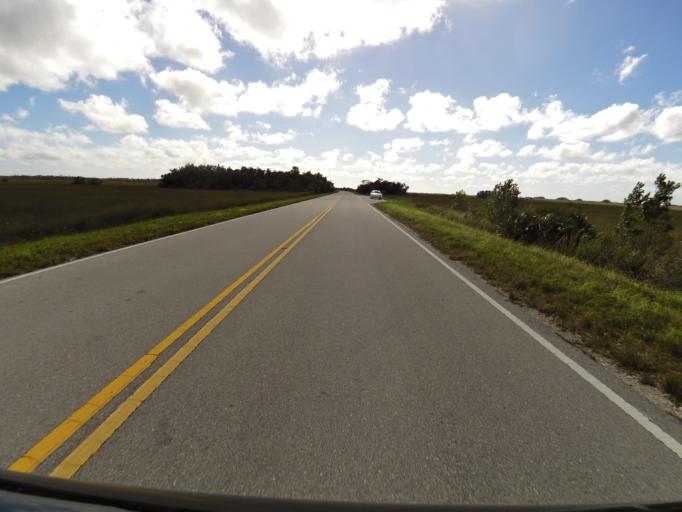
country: US
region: Florida
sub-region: Miami-Dade County
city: Florida City
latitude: 25.3649
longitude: -80.8194
